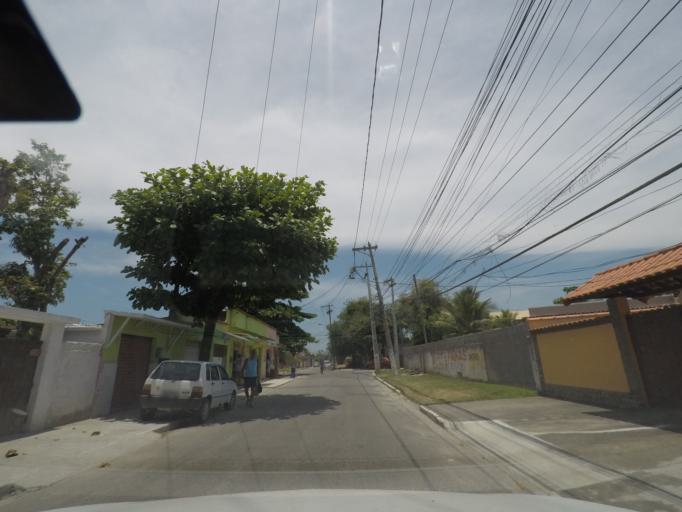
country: BR
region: Rio de Janeiro
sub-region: Marica
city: Marica
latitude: -22.9103
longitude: -42.8390
